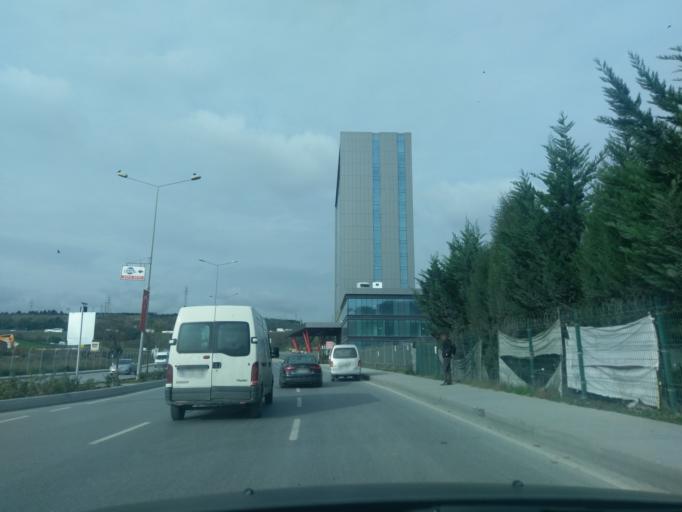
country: TR
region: Istanbul
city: Basaksehir
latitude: 41.0582
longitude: 28.7746
